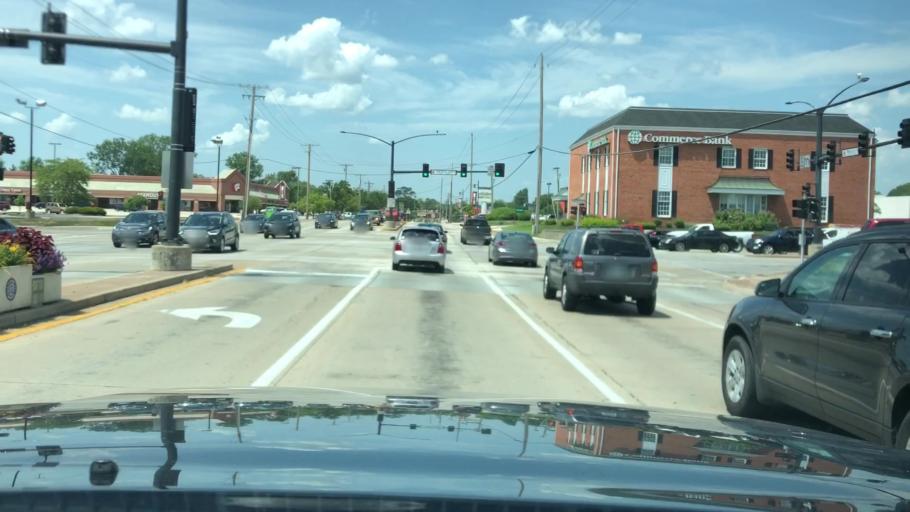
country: US
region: Missouri
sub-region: Saint Charles County
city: Saint Peters
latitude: 38.7884
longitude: -90.6255
